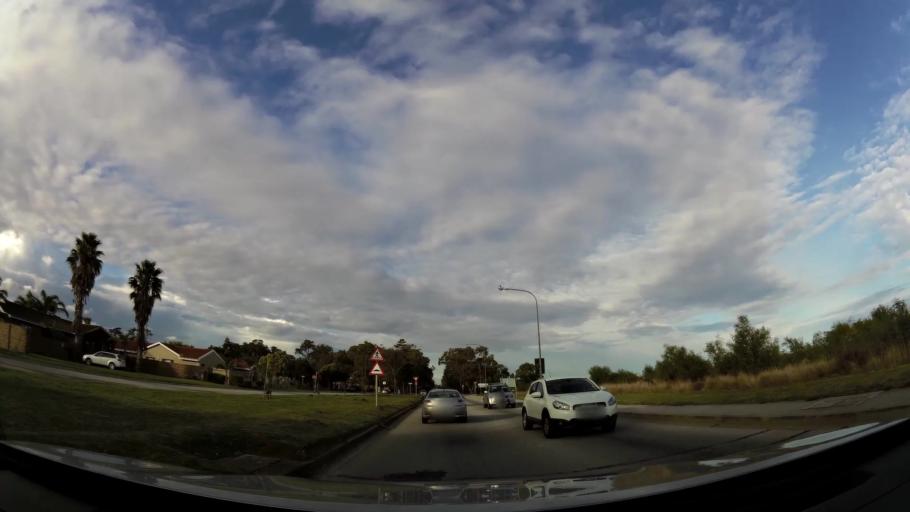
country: ZA
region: Eastern Cape
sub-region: Nelson Mandela Bay Metropolitan Municipality
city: Port Elizabeth
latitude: -33.9584
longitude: 25.4945
